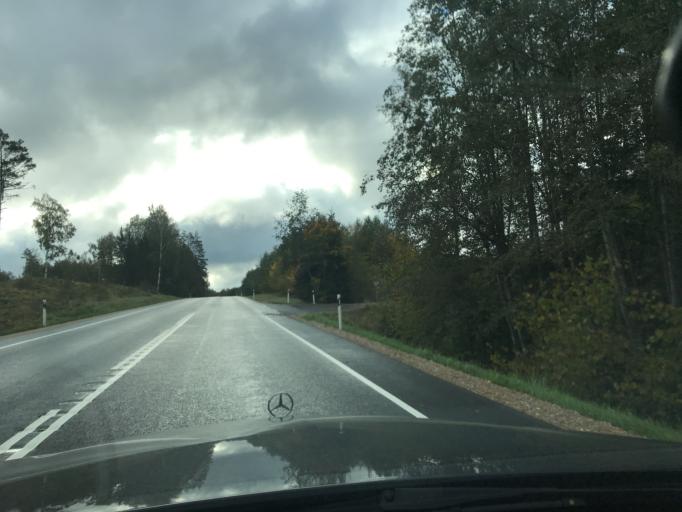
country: EE
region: Viljandimaa
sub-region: Karksi vald
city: Karksi-Nuia
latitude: 58.0588
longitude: 25.6284
